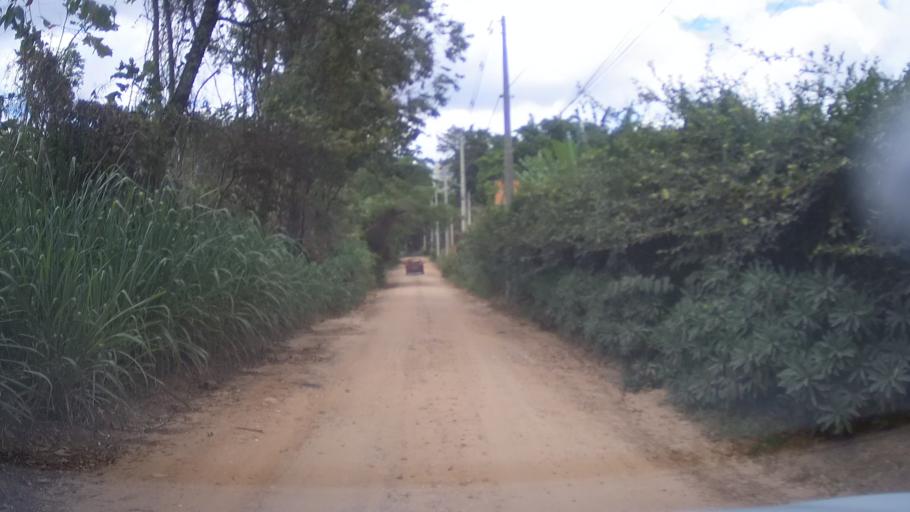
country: BR
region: Sao Paulo
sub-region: Itupeva
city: Itupeva
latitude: -23.1884
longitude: -46.9917
